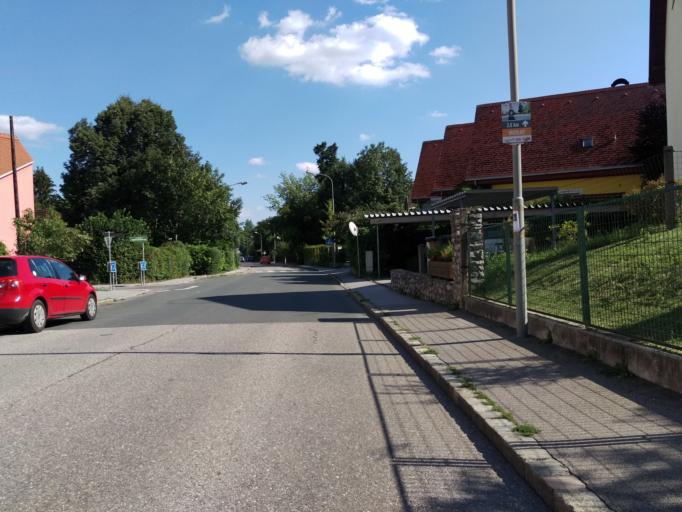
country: AT
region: Styria
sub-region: Graz Stadt
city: Wetzelsdorf
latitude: 47.0628
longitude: 15.3881
